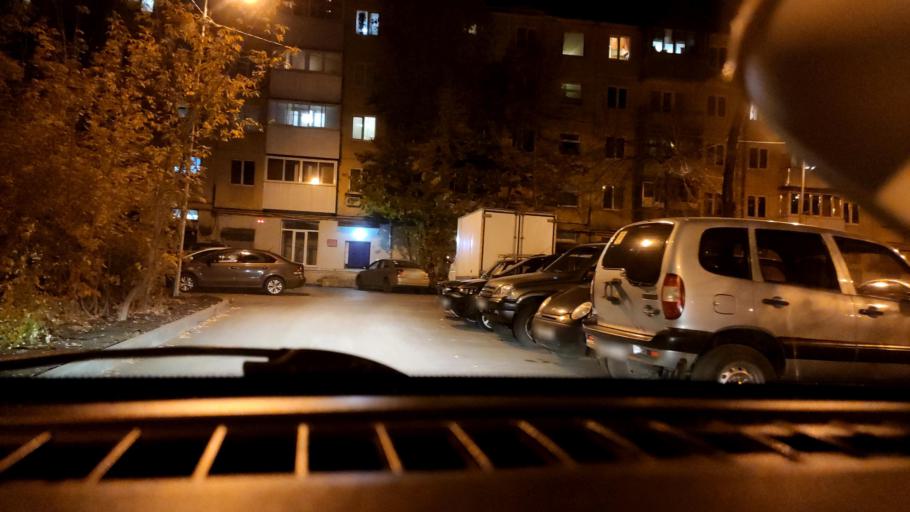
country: RU
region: Samara
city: Samara
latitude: 53.1962
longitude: 50.1774
